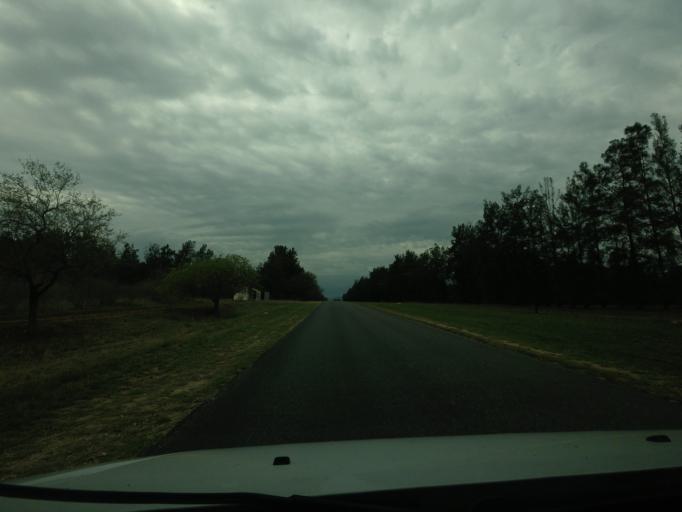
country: ZA
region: Limpopo
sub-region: Mopani District Municipality
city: Hoedspruit
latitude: -24.4416
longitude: 30.8542
